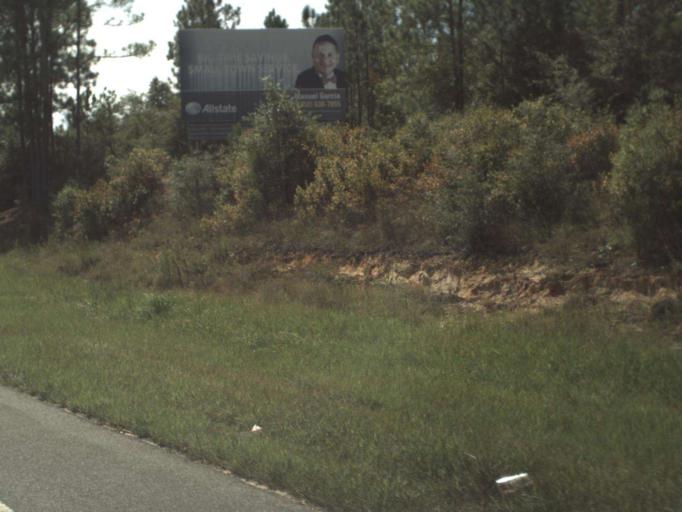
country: US
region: Florida
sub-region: Washington County
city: Chipley
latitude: 30.6399
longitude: -85.5853
